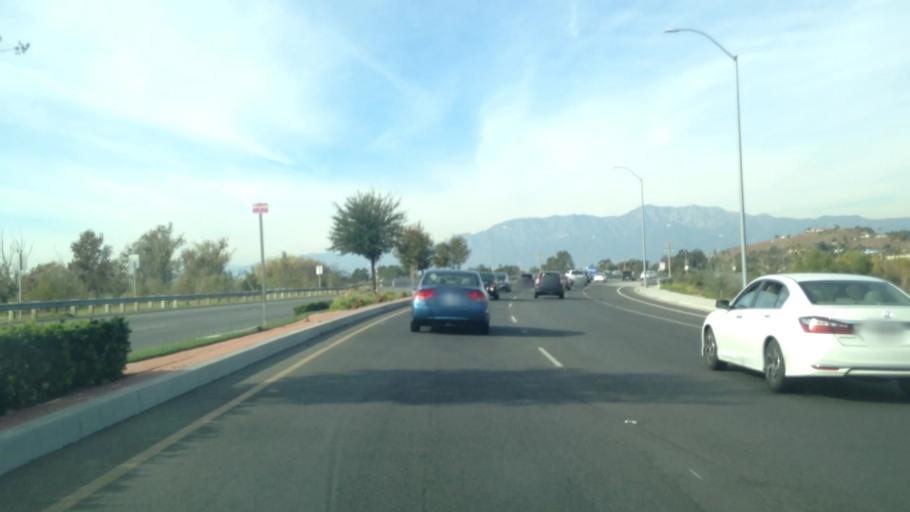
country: US
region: California
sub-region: Riverside County
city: Pedley
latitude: 33.9613
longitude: -117.4646
